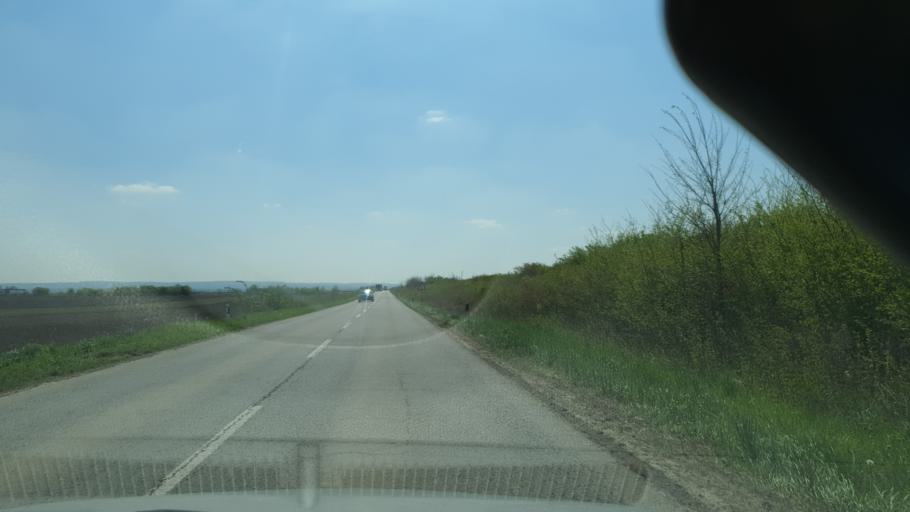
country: RS
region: Autonomna Pokrajina Vojvodina
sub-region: Juznobacki Okrug
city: Backa Palanka
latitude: 45.3072
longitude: 19.4374
